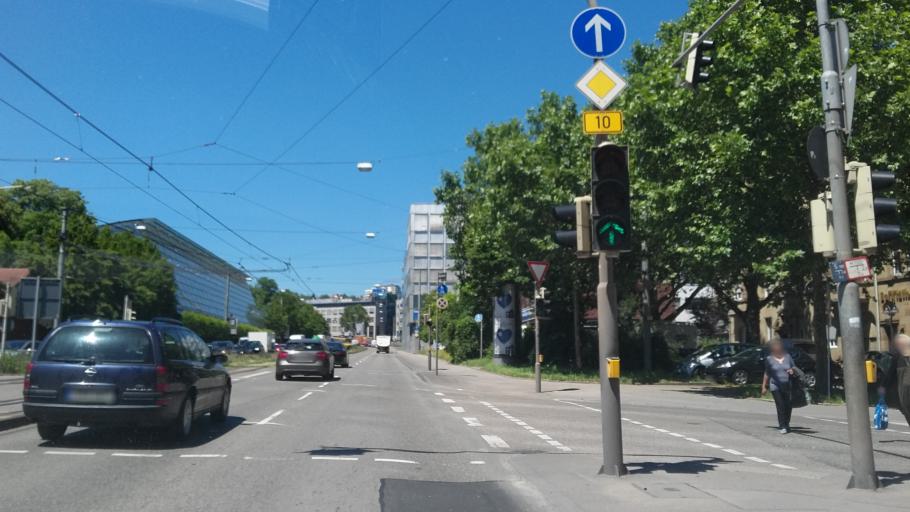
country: DE
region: Baden-Wuerttemberg
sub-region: Regierungsbezirk Stuttgart
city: Stuttgart-Ost
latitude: 48.8060
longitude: 9.2097
